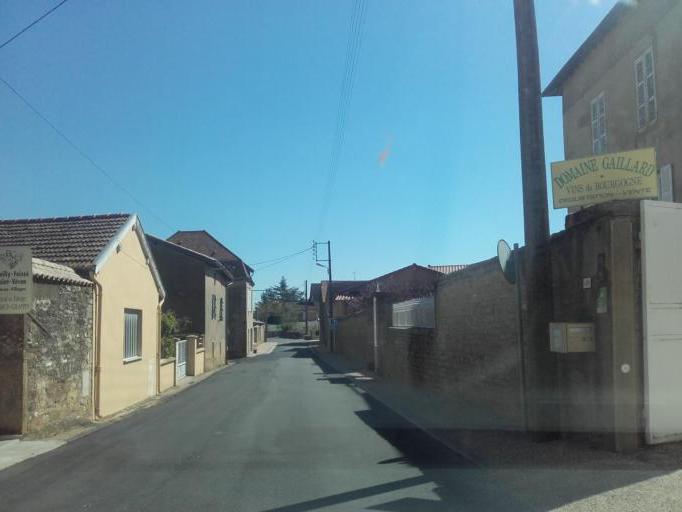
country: FR
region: Bourgogne
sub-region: Departement de Saone-et-Loire
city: Prisse
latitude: 46.3013
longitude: 4.7470
